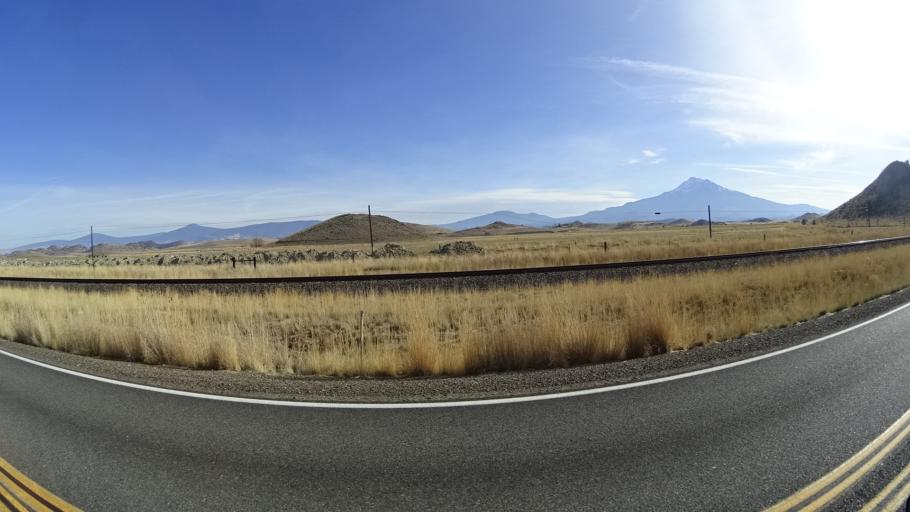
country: US
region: California
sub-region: Siskiyou County
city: Weed
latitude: 41.5395
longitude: -122.5249
